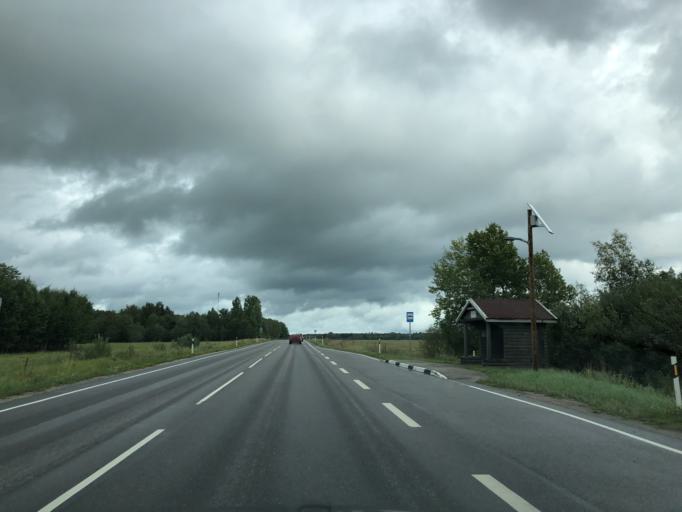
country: EE
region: Laeaene
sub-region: Ridala Parish
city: Uuemoisa
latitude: 58.9625
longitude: 23.8237
